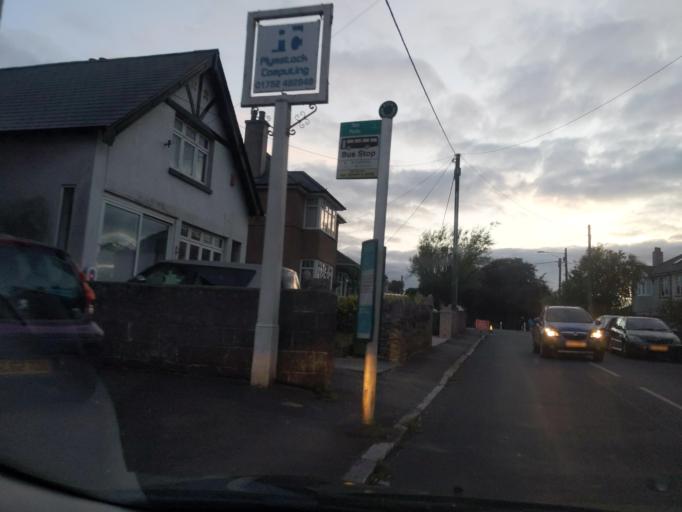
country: GB
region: England
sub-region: Plymouth
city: Plymstock
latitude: 50.3603
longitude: -4.0996
